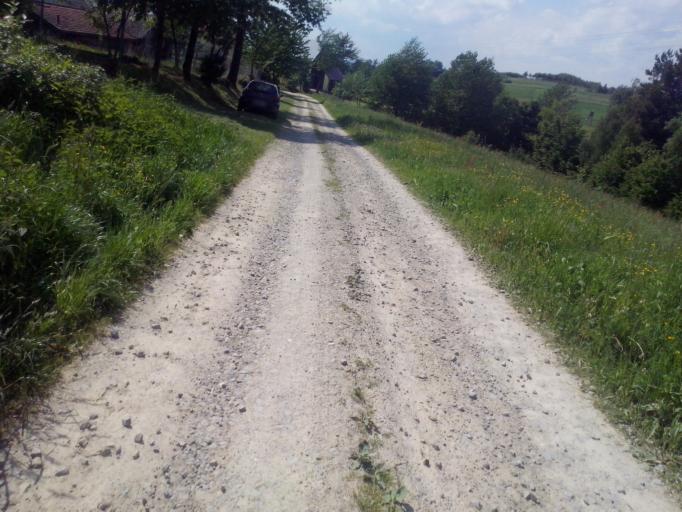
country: PL
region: Subcarpathian Voivodeship
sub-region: Powiat strzyzowski
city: Strzyzow
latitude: 49.8483
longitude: 21.8325
